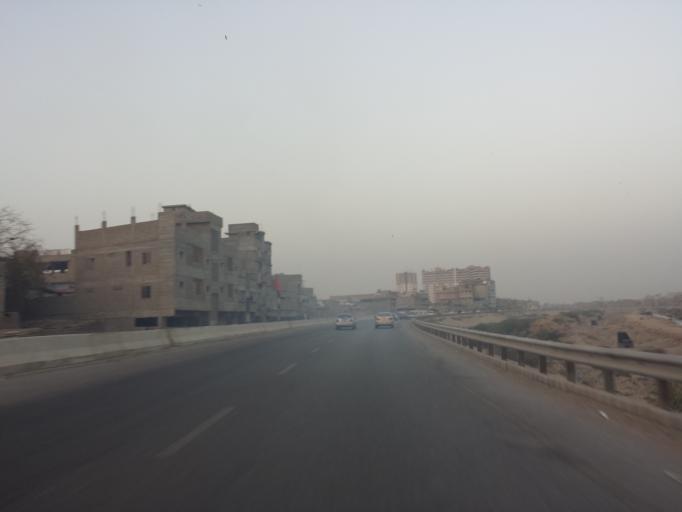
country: PK
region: Sindh
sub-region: Karachi District
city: Karachi
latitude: 24.9105
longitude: 67.0663
